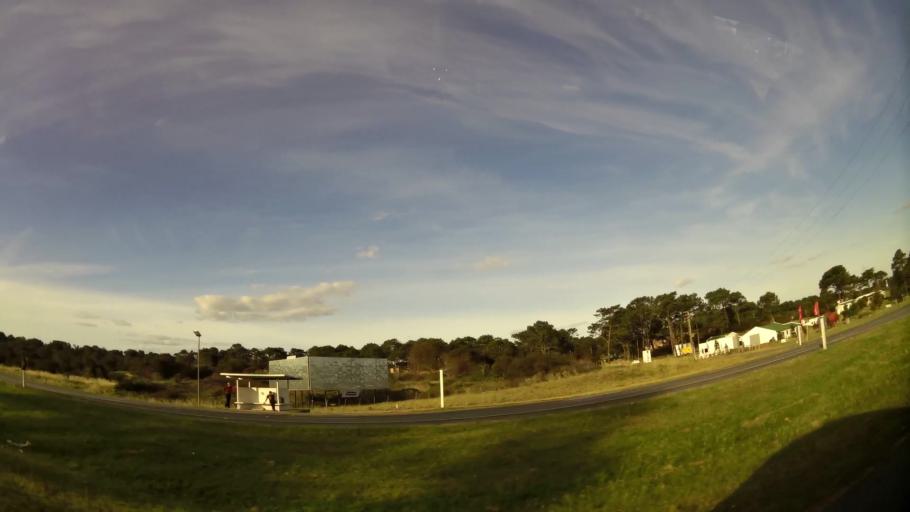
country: UY
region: Maldonado
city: Maldonado
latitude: -34.8734
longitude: -55.0756
